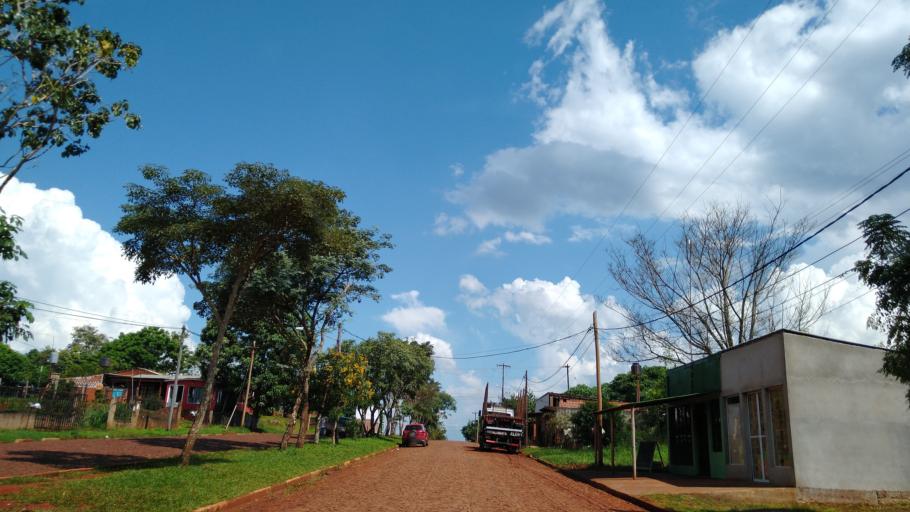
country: AR
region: Misiones
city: Puerto Libertad
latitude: -25.9623
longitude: -54.5603
